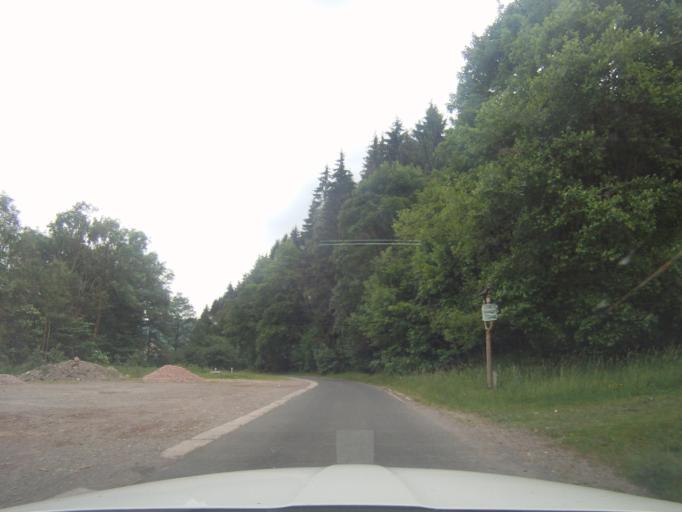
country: DE
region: Thuringia
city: Frauenwald
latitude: 50.5274
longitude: 10.8794
